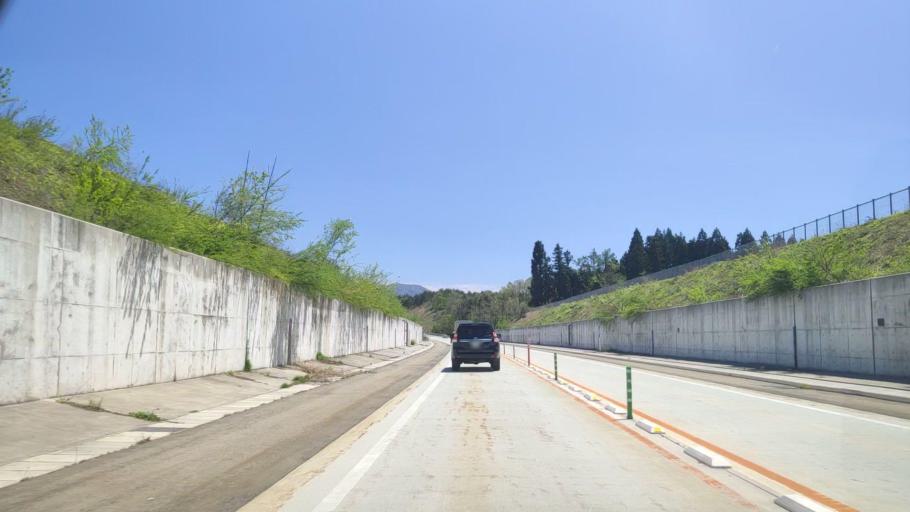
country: JP
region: Yamagata
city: Obanazawa
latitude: 38.5935
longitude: 140.3873
